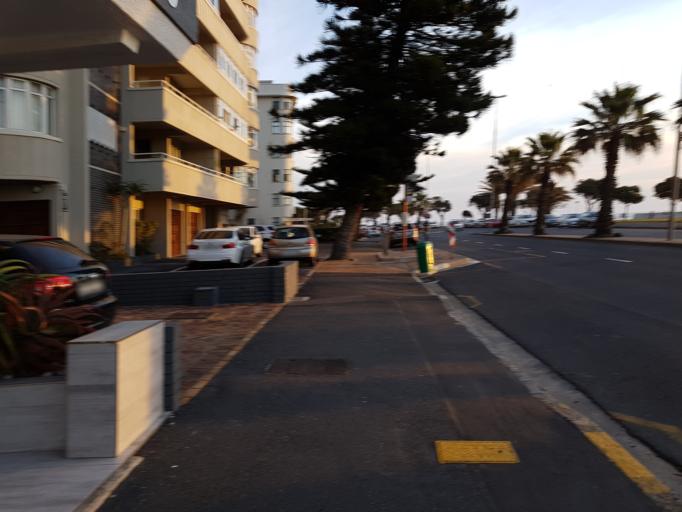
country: ZA
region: Western Cape
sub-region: City of Cape Town
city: Cape Town
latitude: -33.9113
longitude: 18.3900
